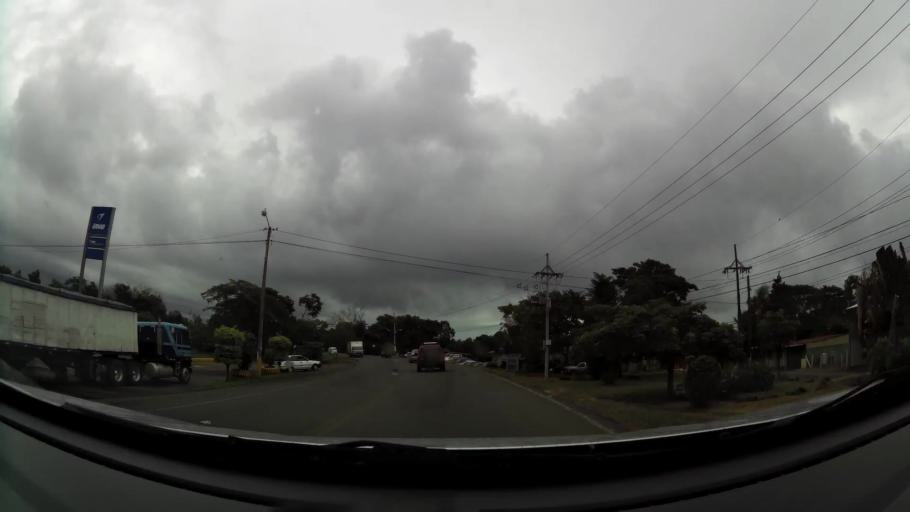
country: CR
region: Puntarenas
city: Esparza
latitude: 9.9961
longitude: -84.6734
